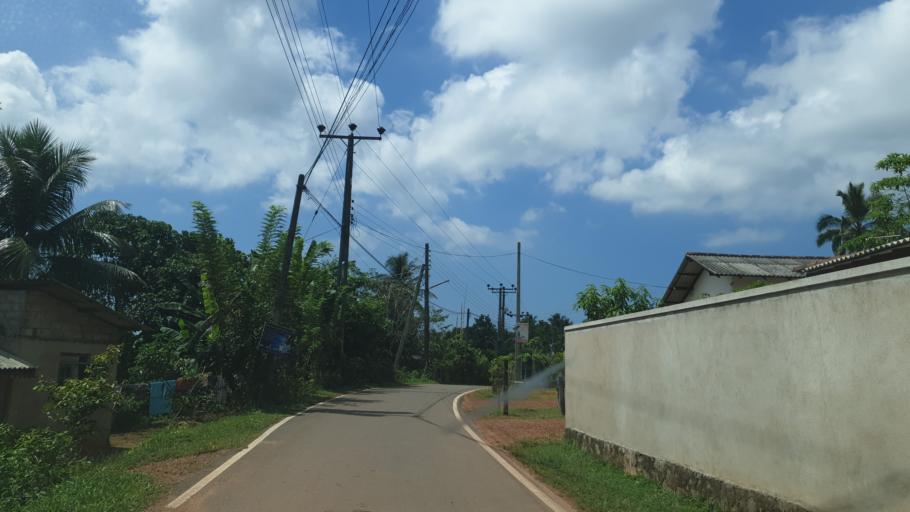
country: LK
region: Western
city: Panadura
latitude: 6.6755
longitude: 79.9664
